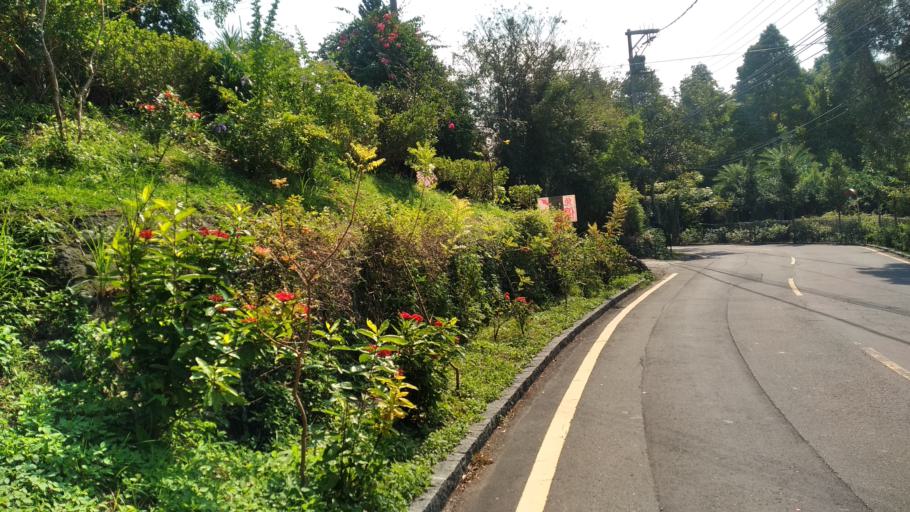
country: TW
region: Taiwan
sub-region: Hsinchu
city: Zhubei
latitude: 24.8542
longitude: 121.1055
